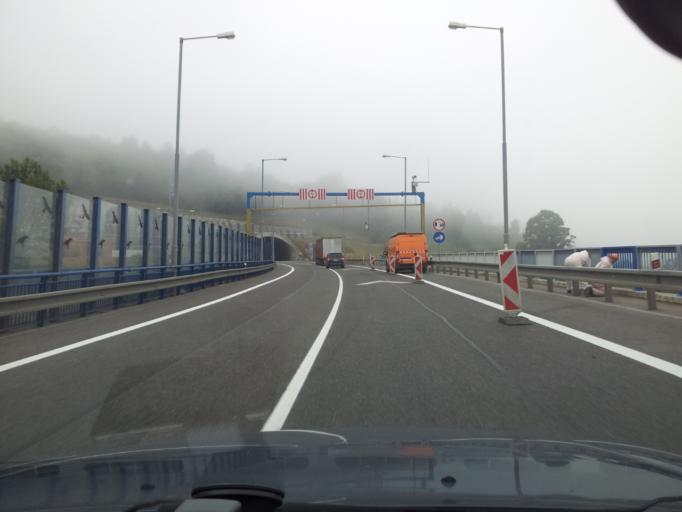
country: SK
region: Zilinsky
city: Cadca
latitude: 49.4348
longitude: 18.7998
